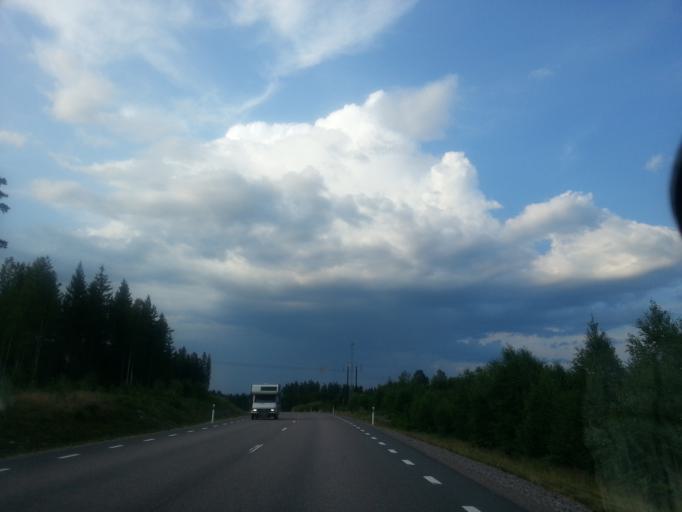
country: SE
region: Dalarna
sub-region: Avesta Kommun
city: Horndal
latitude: 60.3804
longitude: 16.4506
